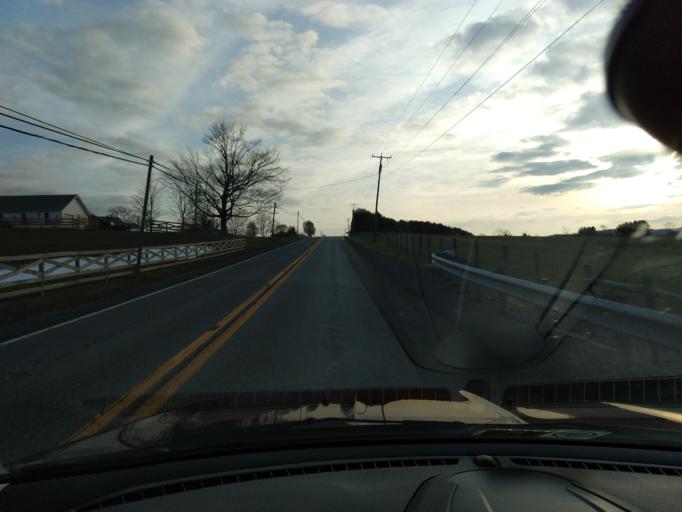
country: US
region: West Virginia
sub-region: Greenbrier County
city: Lewisburg
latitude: 37.9030
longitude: -80.3960
